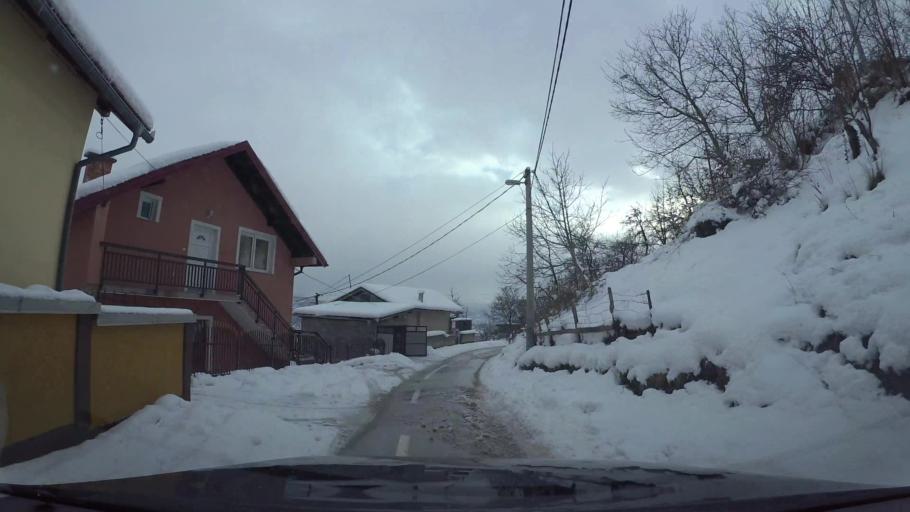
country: BA
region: Federation of Bosnia and Herzegovina
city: Kobilja Glava
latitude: 43.8721
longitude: 18.3891
